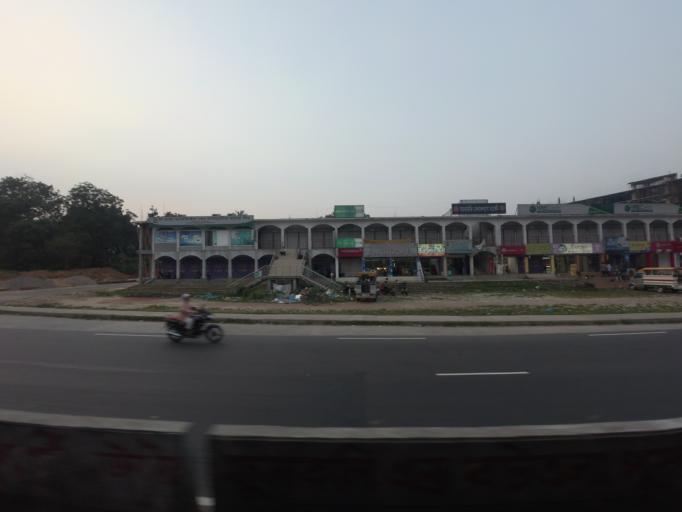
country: BD
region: Chittagong
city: Comilla
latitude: 23.4789
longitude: 91.1170
